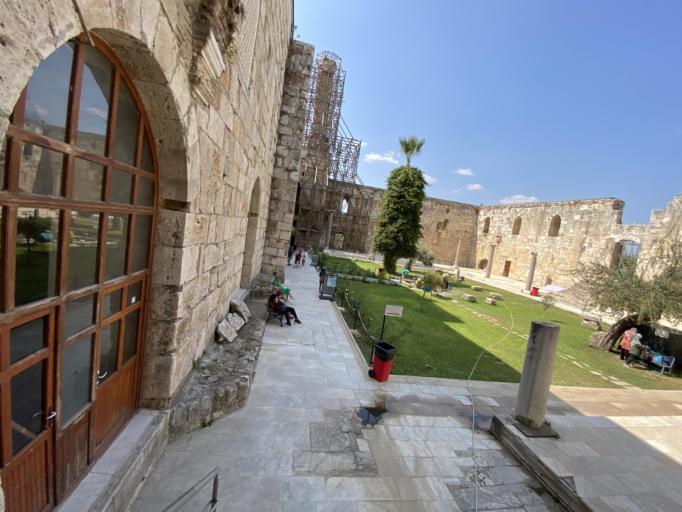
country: TR
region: Izmir
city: Selcuk
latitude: 37.9522
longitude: 27.3662
